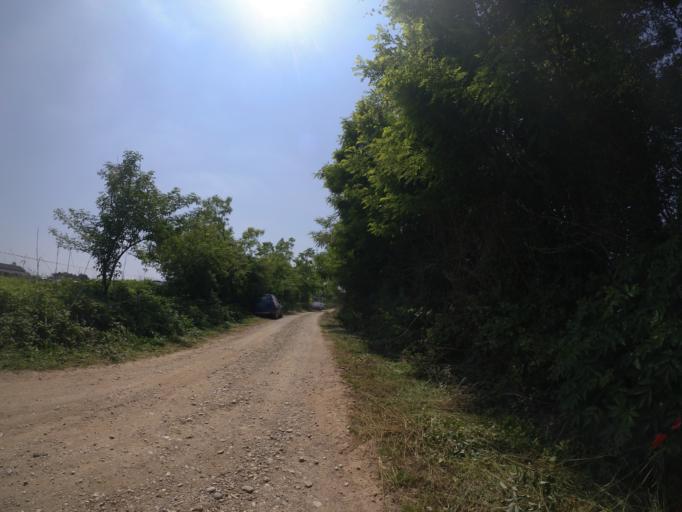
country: IT
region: Friuli Venezia Giulia
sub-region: Provincia di Udine
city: Bertiolo
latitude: 45.9609
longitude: 13.0876
